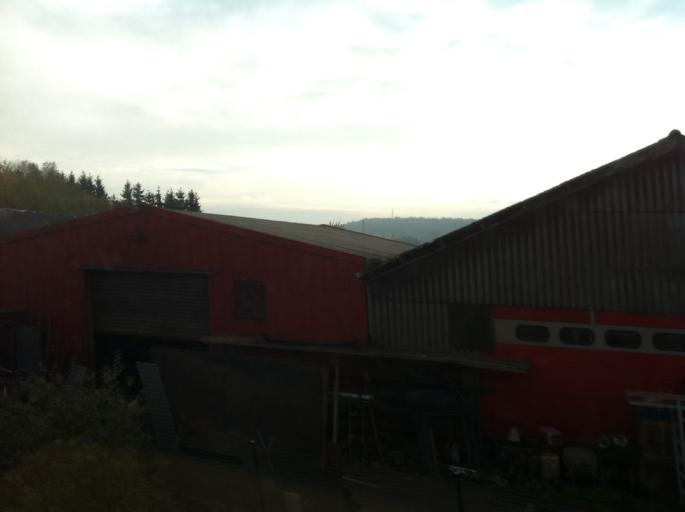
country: FR
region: Lorraine
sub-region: Departement de la Moselle
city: Russange
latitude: 49.4981
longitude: 5.9495
